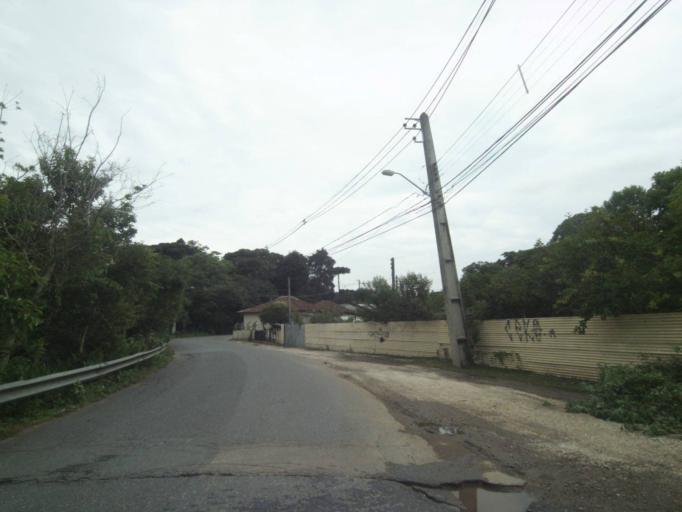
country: BR
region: Parana
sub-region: Curitiba
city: Curitiba
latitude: -25.4138
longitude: -49.3081
